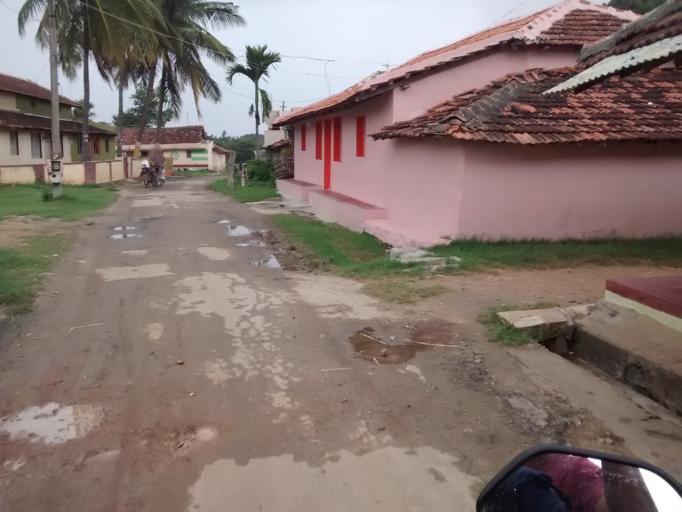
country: IN
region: Karnataka
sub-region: Hassan
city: Hassan
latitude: 12.9482
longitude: 76.1426
